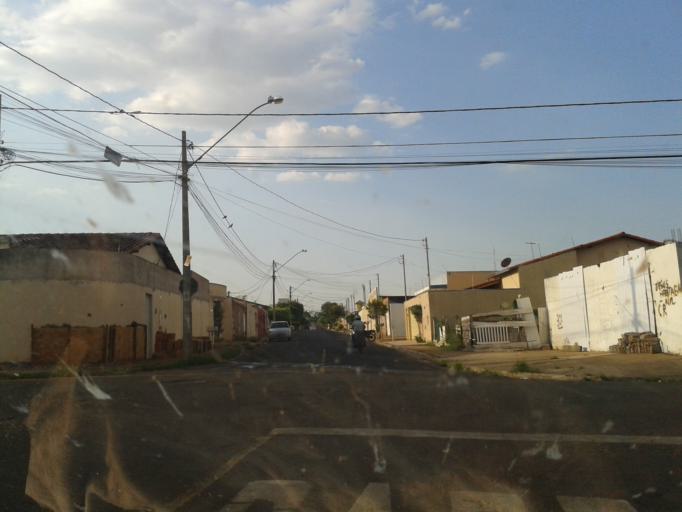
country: BR
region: Minas Gerais
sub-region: Uberlandia
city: Uberlandia
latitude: -18.9607
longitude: -48.3116
